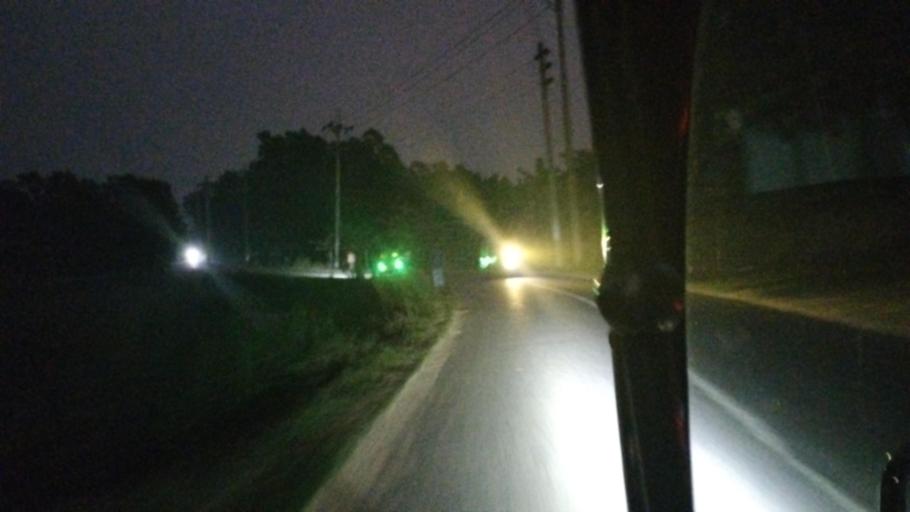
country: BD
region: Dhaka
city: Gafargaon
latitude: 24.4017
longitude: 90.3603
